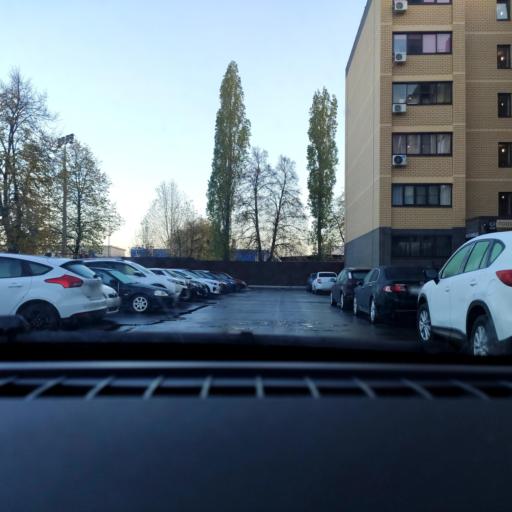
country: RU
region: Voronezj
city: Voronezh
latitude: 51.6671
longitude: 39.2796
